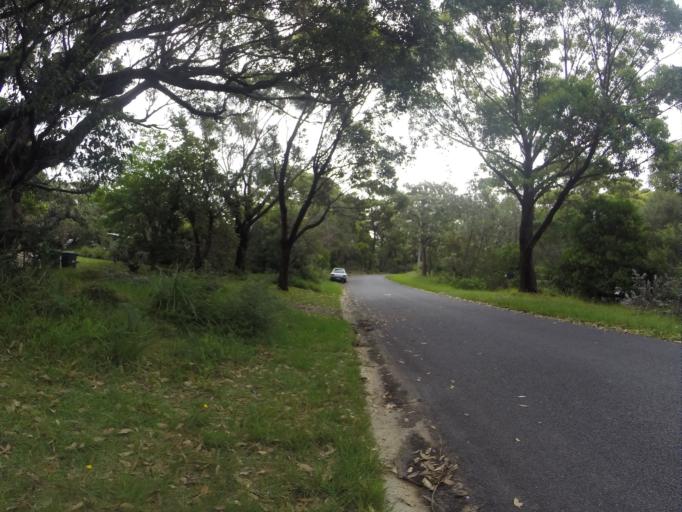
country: AU
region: New South Wales
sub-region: Eurobodalla
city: Broulee
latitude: -35.8307
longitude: 150.2283
